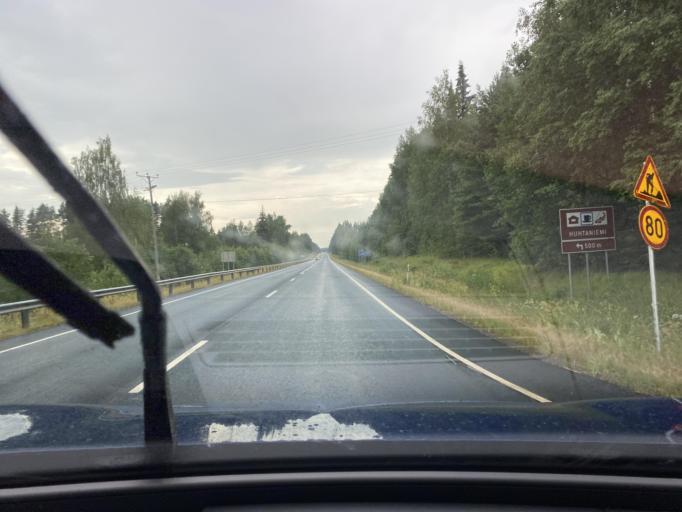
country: FI
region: Central Ostrobothnia
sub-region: Kaustinen
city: Veteli
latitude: 63.4186
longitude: 23.9397
